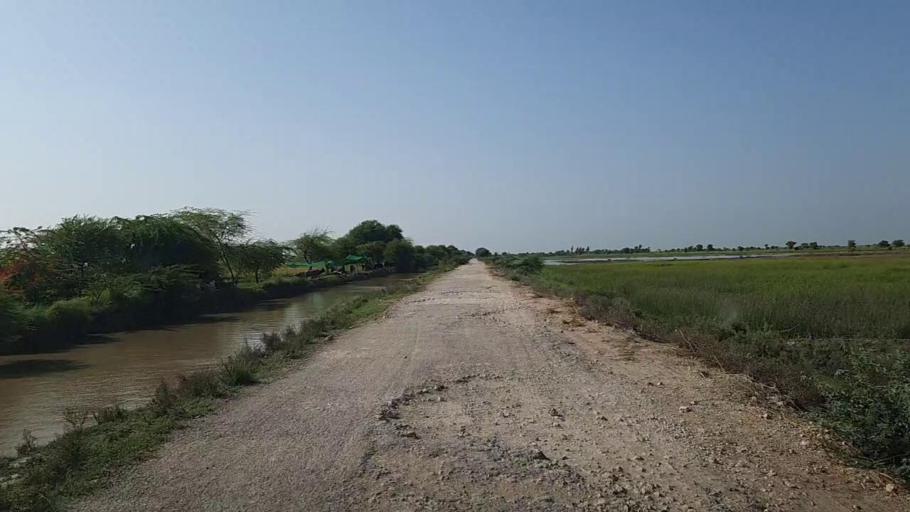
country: PK
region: Sindh
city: Kario
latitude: 24.7957
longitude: 68.5585
